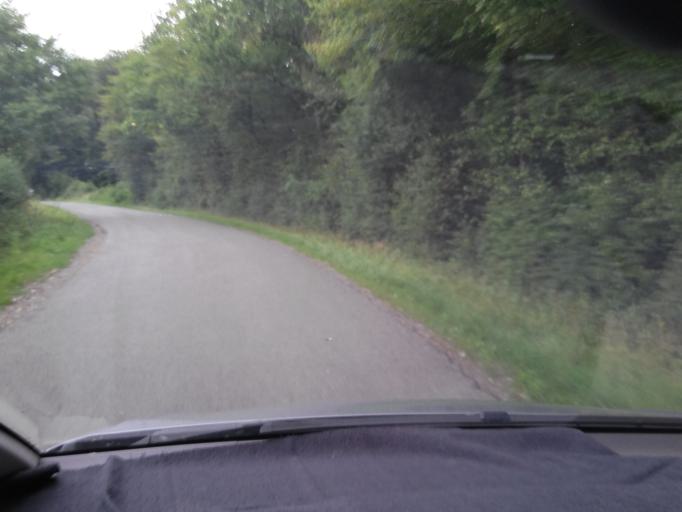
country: BE
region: Wallonia
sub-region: Province du Luxembourg
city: Attert
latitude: 49.7507
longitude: 5.8104
